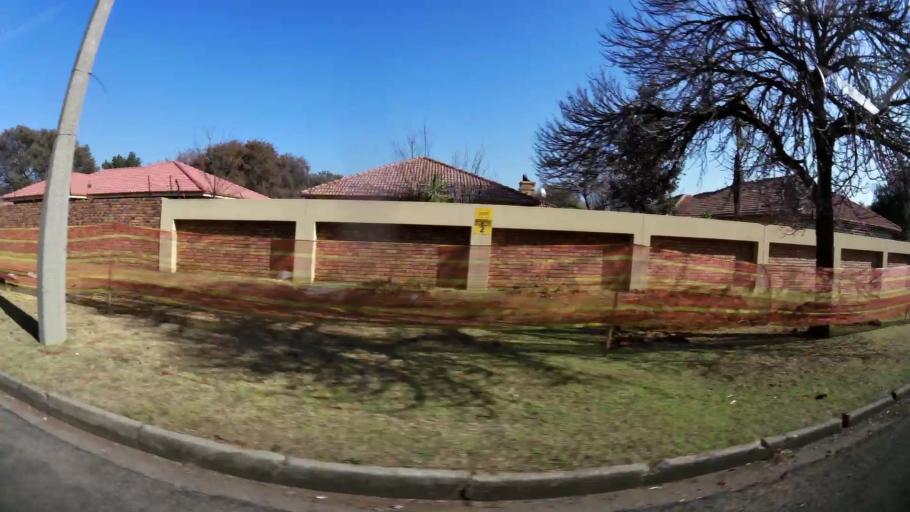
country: ZA
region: Gauteng
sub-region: Ekurhuleni Metropolitan Municipality
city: Benoni
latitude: -26.1516
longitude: 28.3088
